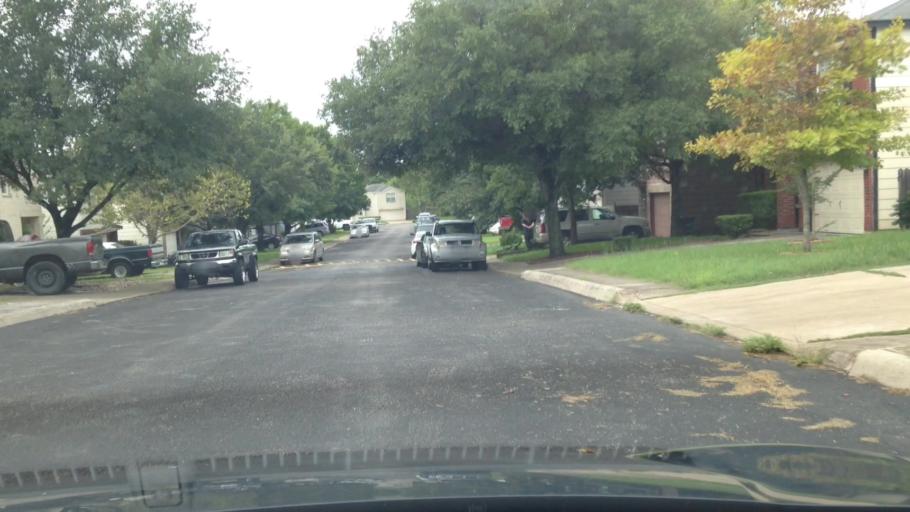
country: US
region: Texas
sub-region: Bexar County
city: Windcrest
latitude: 29.5704
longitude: -98.4151
